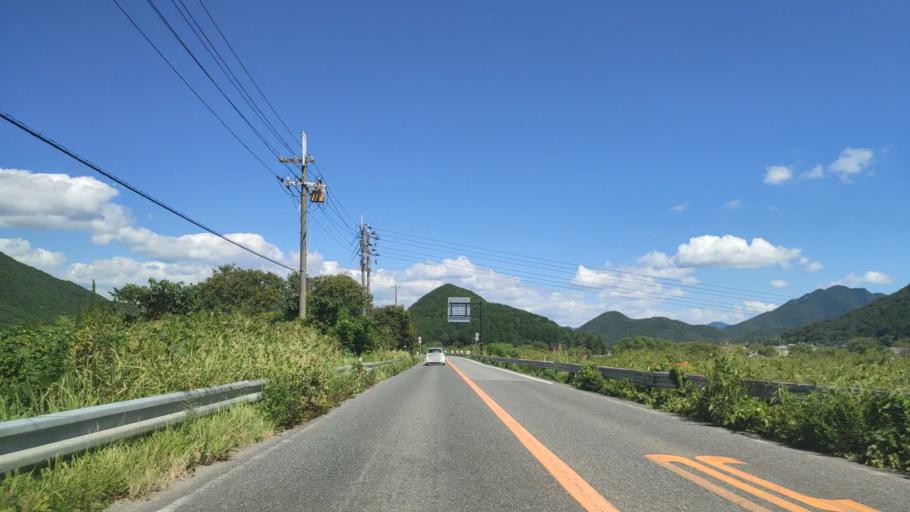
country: JP
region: Hyogo
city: Nishiwaki
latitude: 35.0244
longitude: 134.9842
